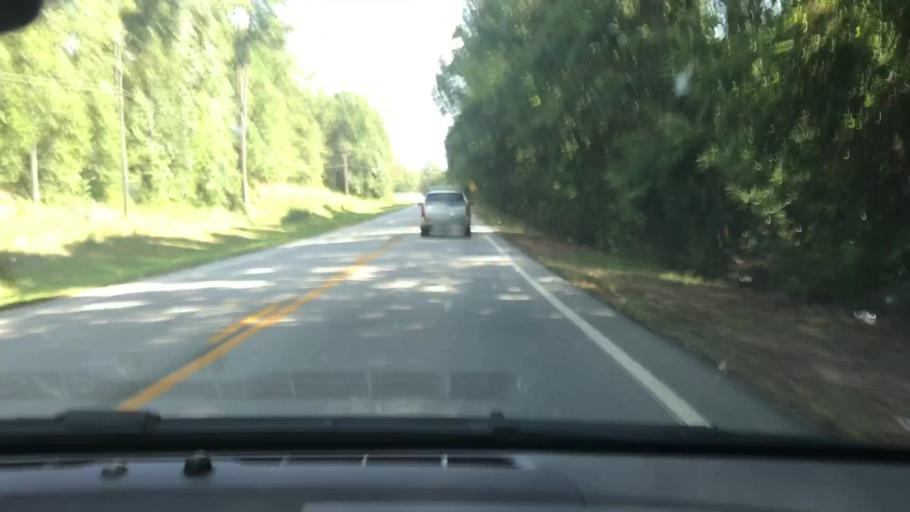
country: US
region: Georgia
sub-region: Troup County
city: La Grange
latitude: 33.0900
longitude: -85.0574
